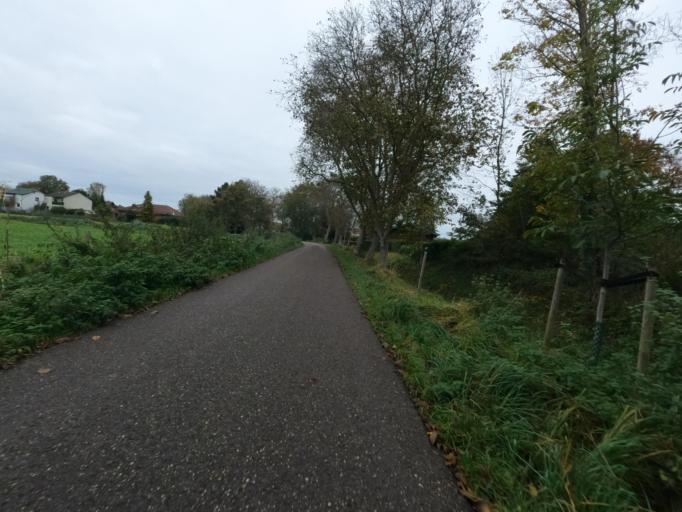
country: DE
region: North Rhine-Westphalia
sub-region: Regierungsbezirk Koln
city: Linnich
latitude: 50.9589
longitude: 6.3123
